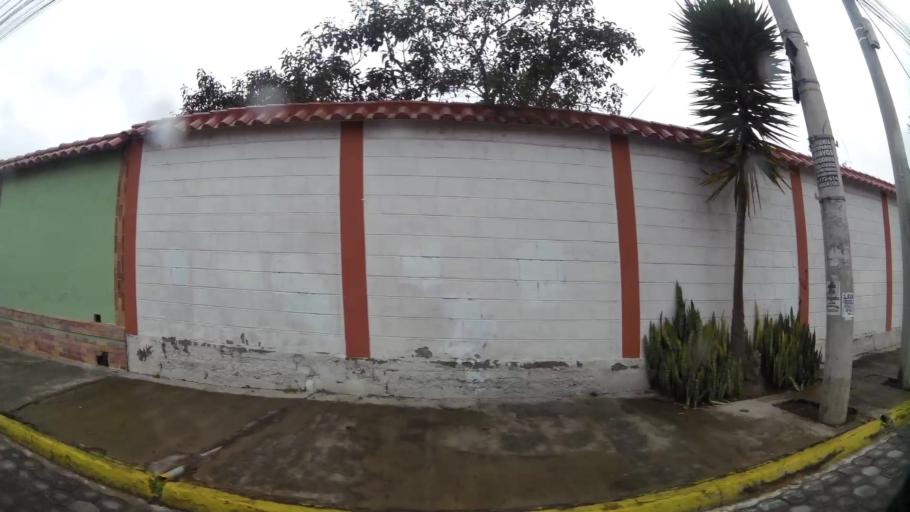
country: EC
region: Pichincha
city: Sangolqui
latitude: -0.2743
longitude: -78.4657
